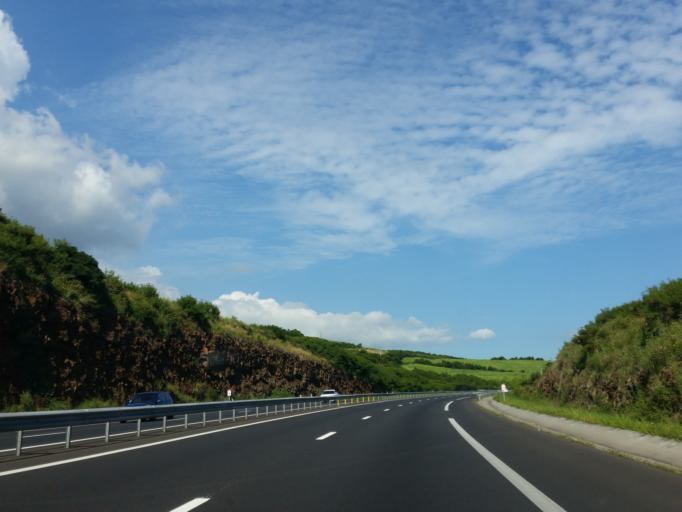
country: RE
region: Reunion
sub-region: Reunion
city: Trois-Bassins
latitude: -21.0810
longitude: 55.2551
